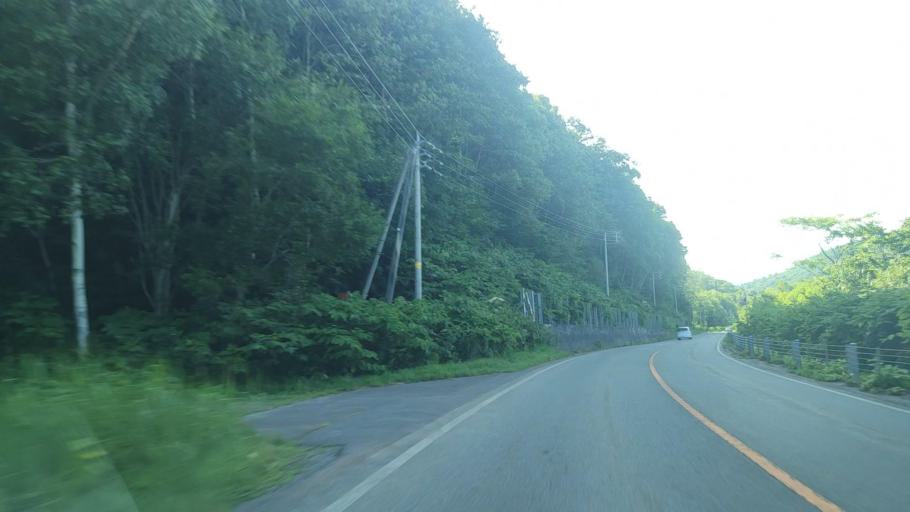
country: JP
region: Hokkaido
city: Nayoro
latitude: 44.7219
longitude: 142.2439
